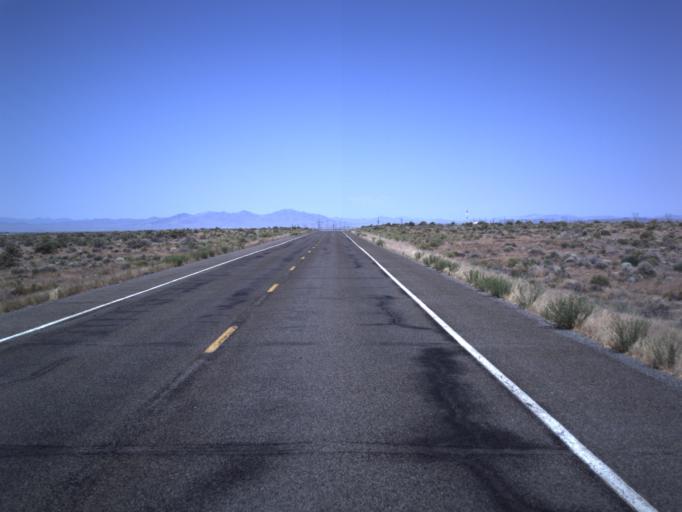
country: US
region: Utah
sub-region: Millard County
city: Delta
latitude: 39.4884
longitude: -112.5479
